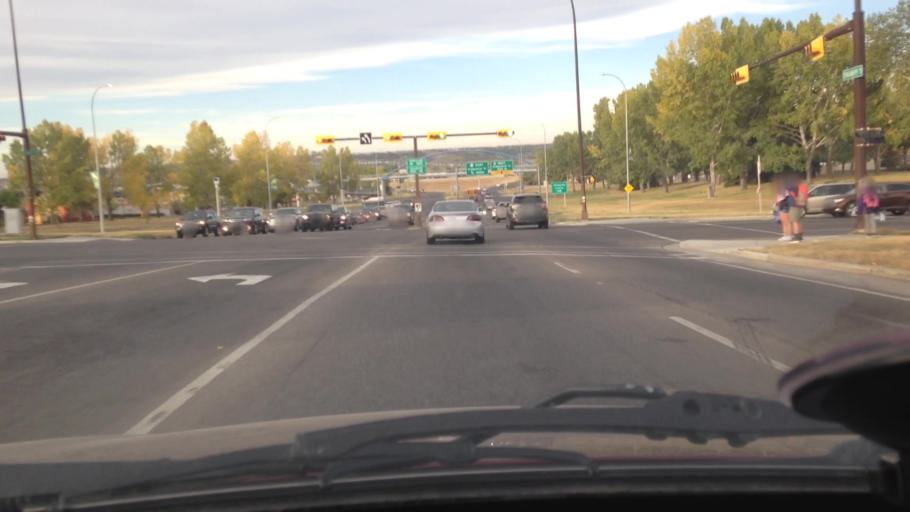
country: CA
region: Alberta
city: Calgary
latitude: 51.1029
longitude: -114.1424
